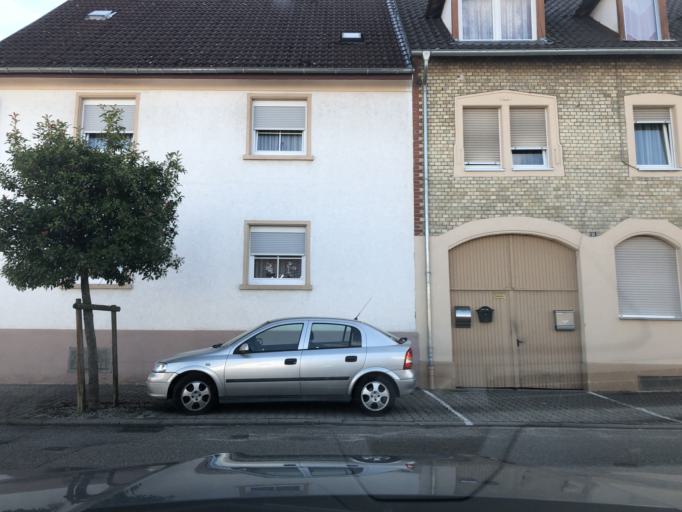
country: DE
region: Baden-Wuerttemberg
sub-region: Karlsruhe Region
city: Kronau
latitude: 49.2228
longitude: 8.6331
